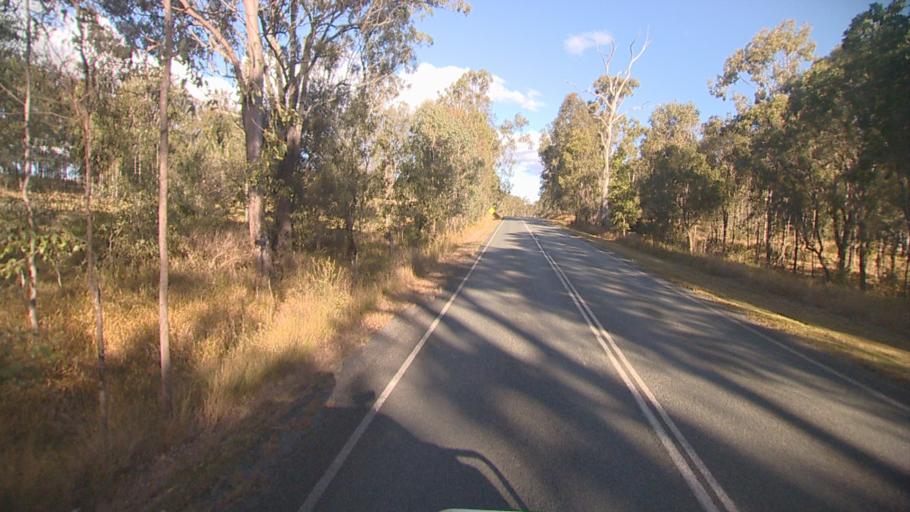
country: AU
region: Queensland
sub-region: Logan
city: Cedar Vale
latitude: -27.8987
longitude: 153.0892
